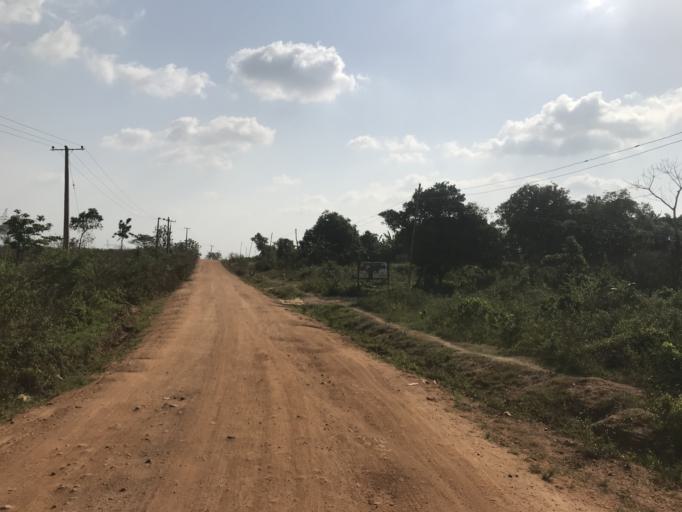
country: NG
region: Osun
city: Osogbo
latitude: 7.8400
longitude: 4.5722
